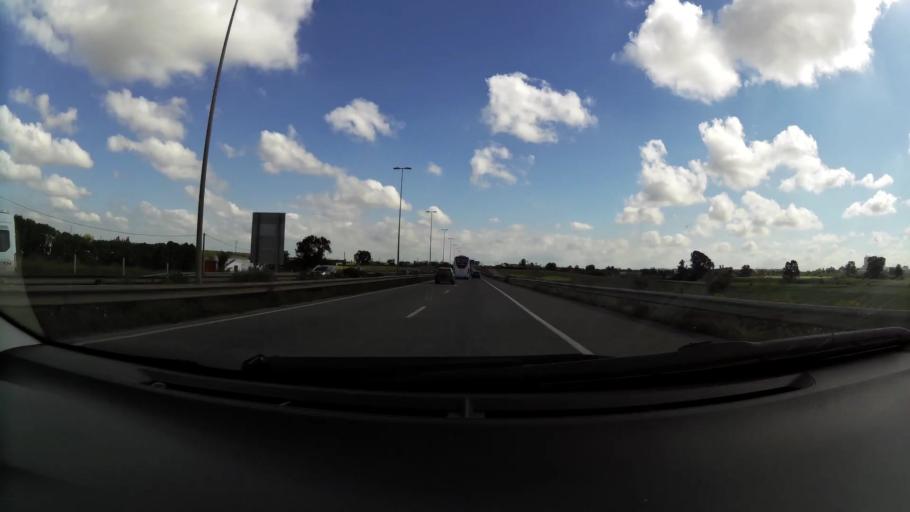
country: MA
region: Grand Casablanca
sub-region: Nouaceur
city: Bouskoura
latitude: 33.4475
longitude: -7.6330
